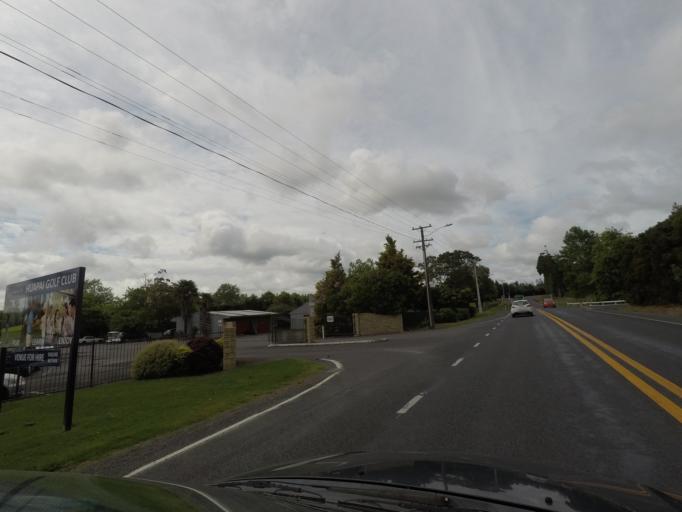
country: NZ
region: Auckland
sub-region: Auckland
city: Rosebank
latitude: -36.7743
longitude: 174.5872
